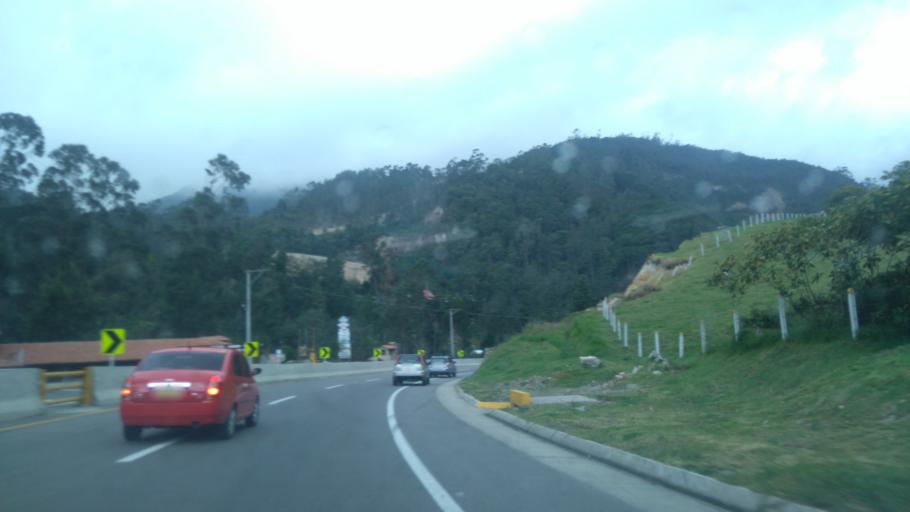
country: CO
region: Cundinamarca
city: El Rosal
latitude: 4.9003
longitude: -74.3110
